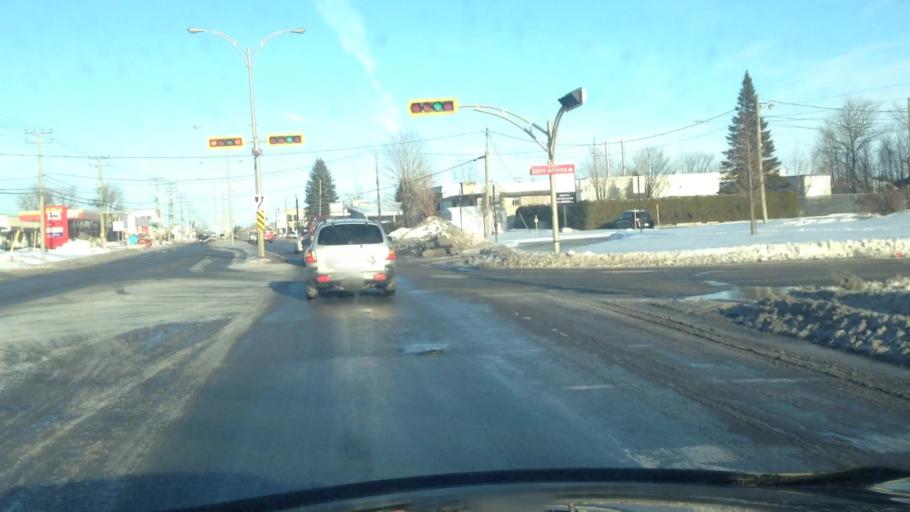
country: CA
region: Quebec
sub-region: Laurentides
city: Saint-Jerome
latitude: 45.7661
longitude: -73.9788
